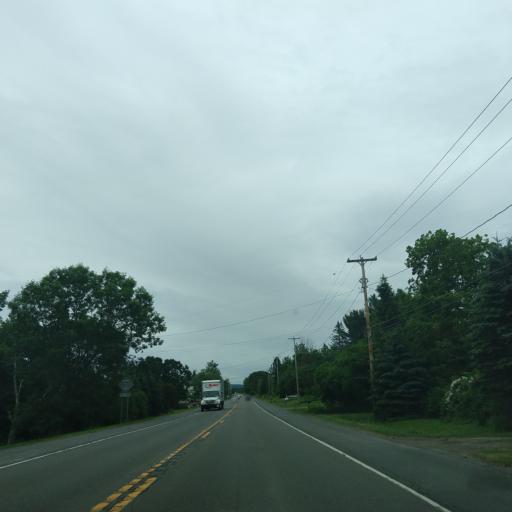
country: US
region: New York
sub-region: Tompkins County
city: Dryden
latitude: 42.4822
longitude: -76.3670
